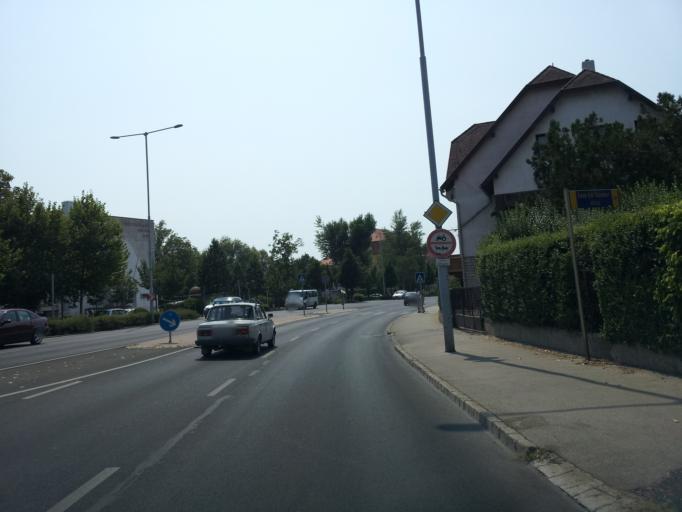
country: HU
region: Veszprem
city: Balatonfured
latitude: 46.9517
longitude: 17.8881
